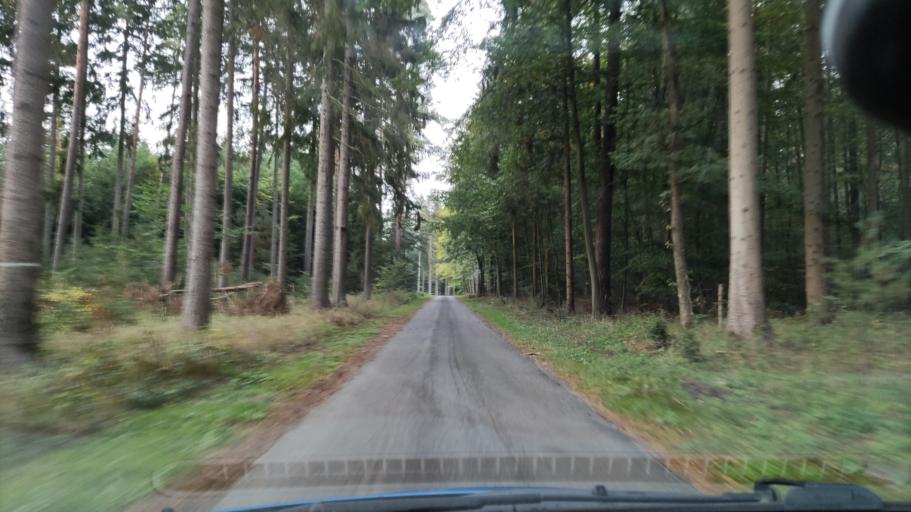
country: DE
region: Lower Saxony
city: Karwitz
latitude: 53.0830
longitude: 10.9735
